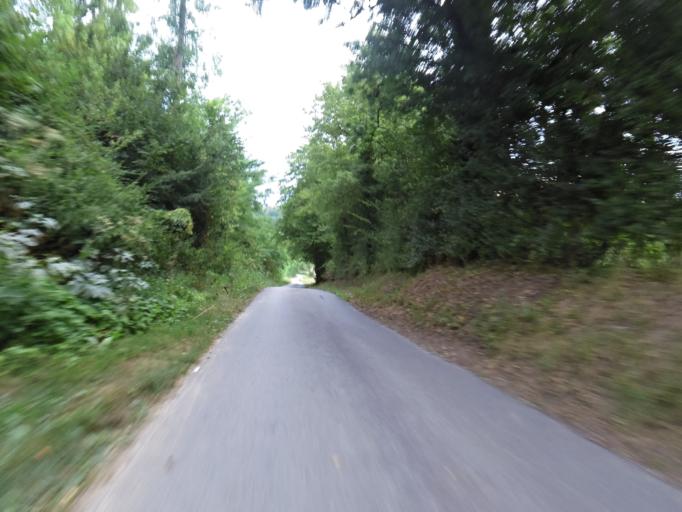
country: FR
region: Rhone-Alpes
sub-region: Departement de l'Ain
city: Perouges
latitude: 45.9226
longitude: 5.1733
